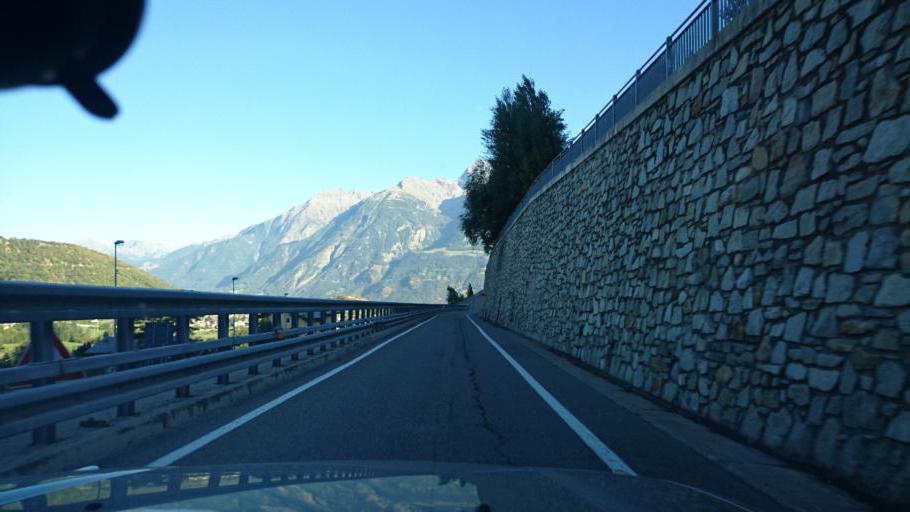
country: IT
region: Aosta Valley
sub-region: Valle d'Aosta
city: La Cretaz-Roisan
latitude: 45.7640
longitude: 7.3125
